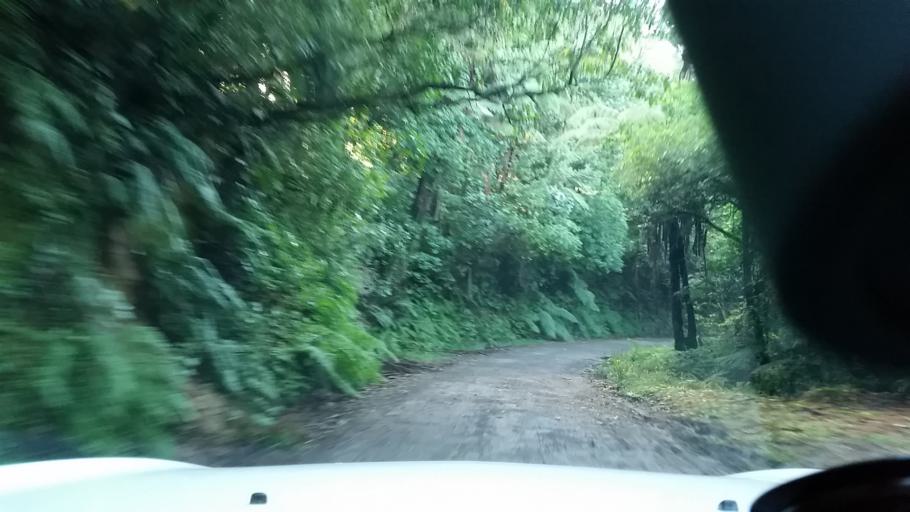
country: NZ
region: Bay of Plenty
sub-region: Kawerau District
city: Kawerau
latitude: -38.0190
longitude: 176.5803
